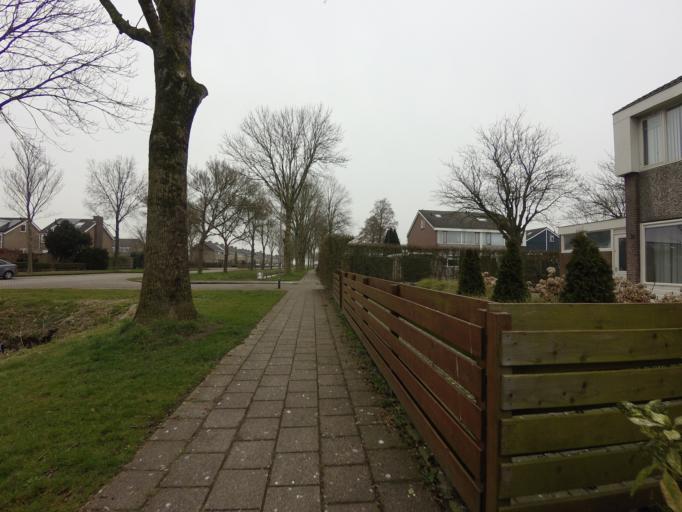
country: NL
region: Friesland
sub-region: Gemeente Franekeradeel
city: Franeker
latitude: 53.1902
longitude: 5.5615
